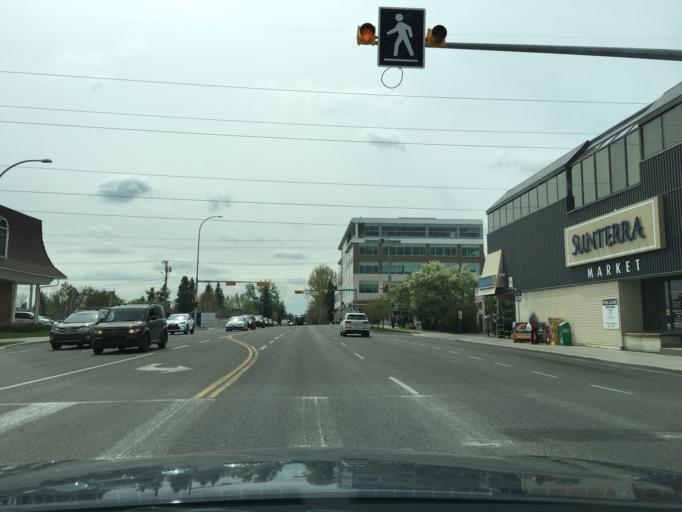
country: CA
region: Alberta
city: Calgary
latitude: 51.0096
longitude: -114.0814
